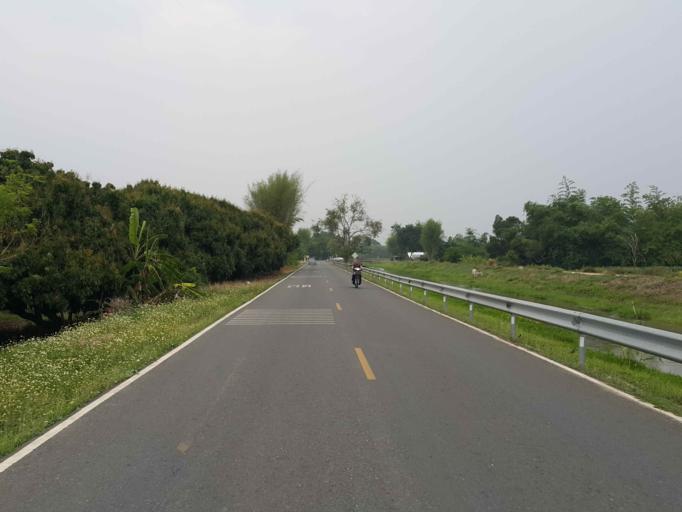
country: TH
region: Chiang Mai
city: San Sai
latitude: 18.9780
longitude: 98.9852
